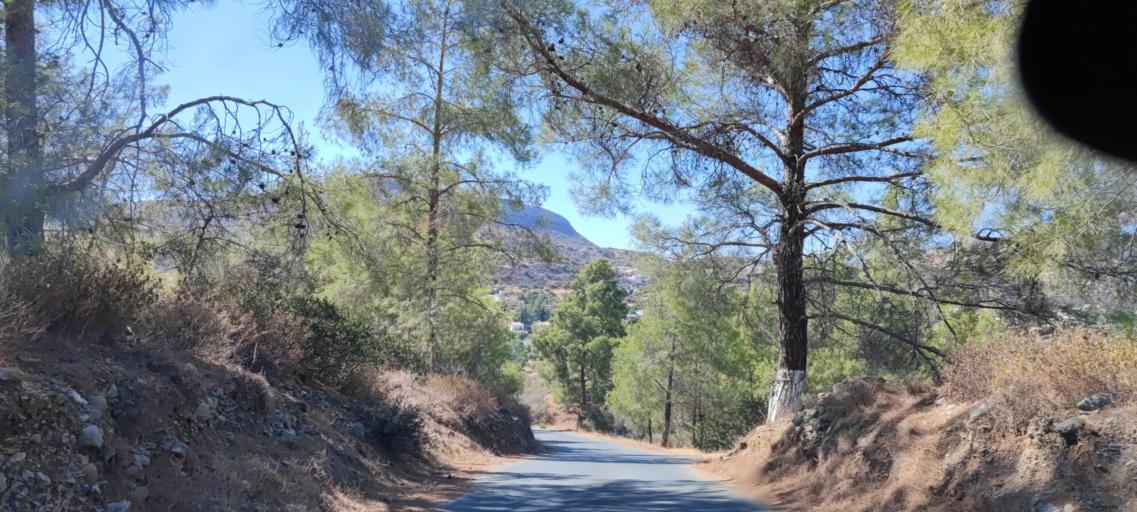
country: CY
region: Limassol
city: Mouttagiaka
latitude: 34.7558
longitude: 33.1081
